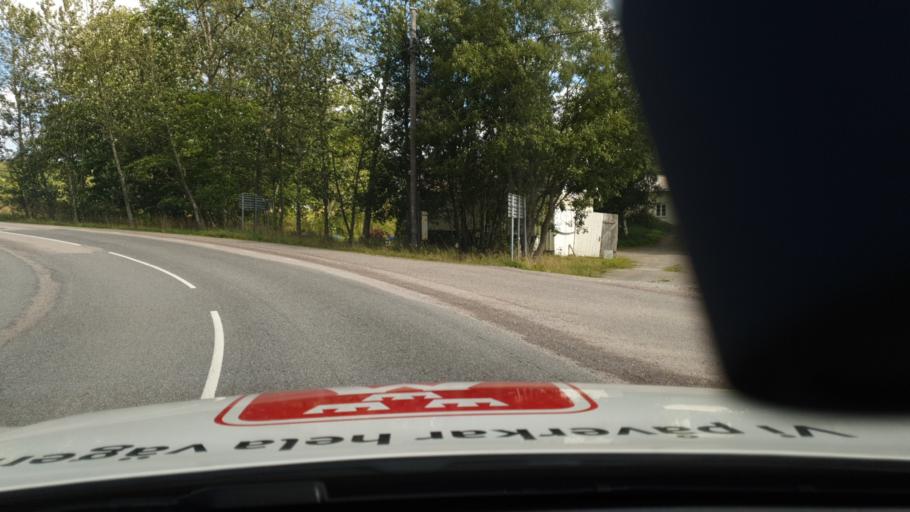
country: SE
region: Vaestra Goetaland
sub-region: Orust
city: Henan
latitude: 58.2214
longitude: 11.6112
